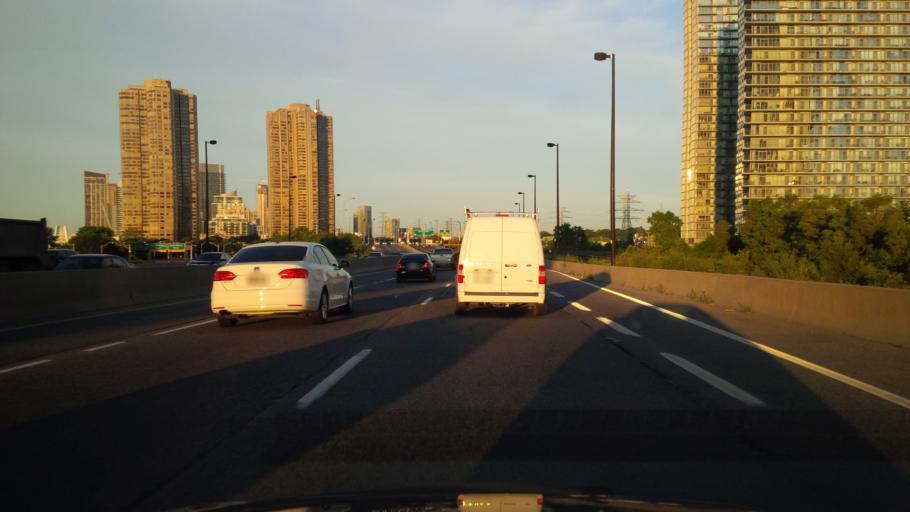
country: CA
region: Ontario
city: Toronto
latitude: 43.6365
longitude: -79.4674
